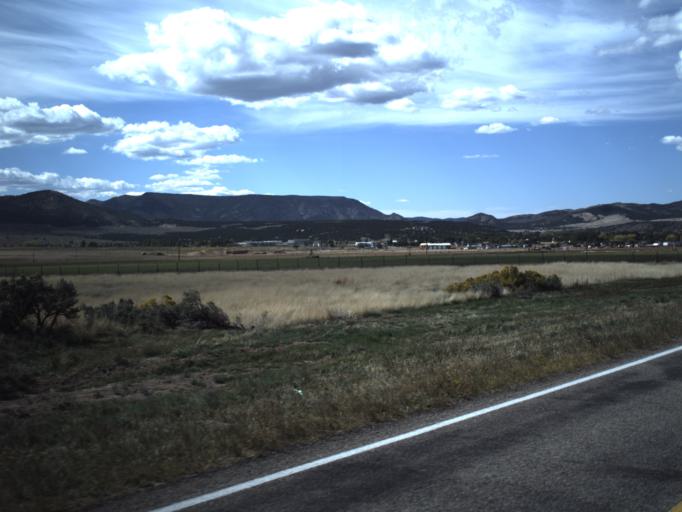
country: US
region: Utah
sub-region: Washington County
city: Enterprise
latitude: 37.5660
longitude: -113.6939
